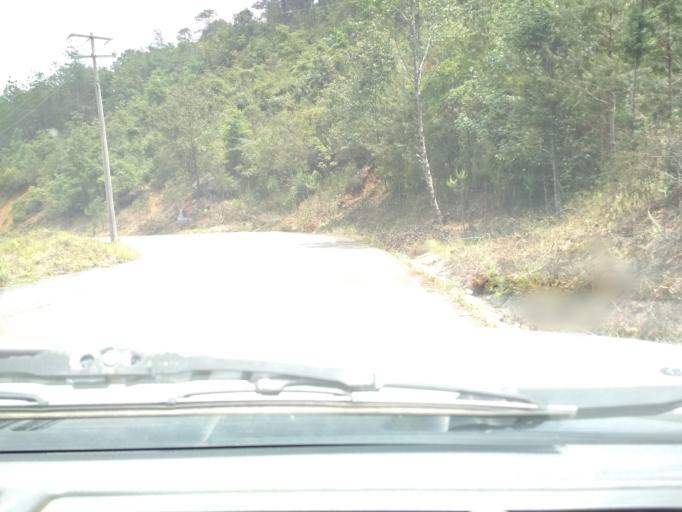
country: MX
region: Veracruz
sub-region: Camerino Z. Mendoza
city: Necoxtla
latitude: 18.7864
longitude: -97.1553
